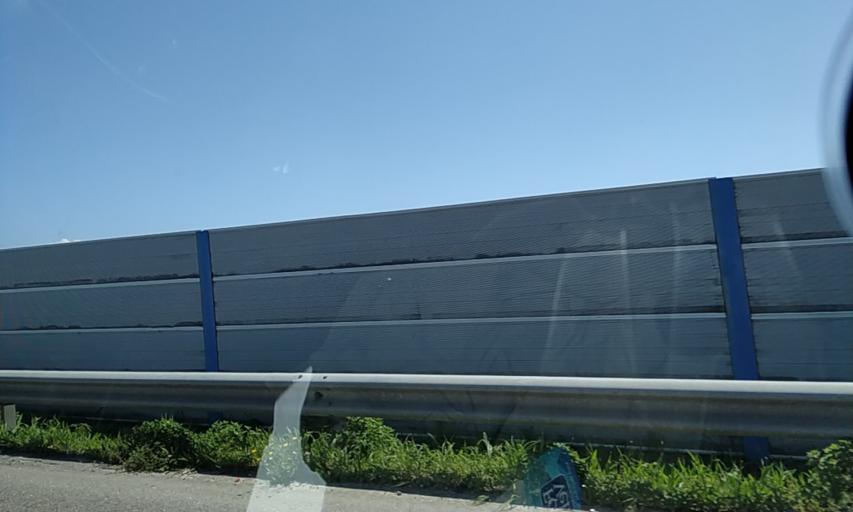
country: PT
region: Aveiro
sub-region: Ilhavo
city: Gafanha da Nazare
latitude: 40.6292
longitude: -8.6995
